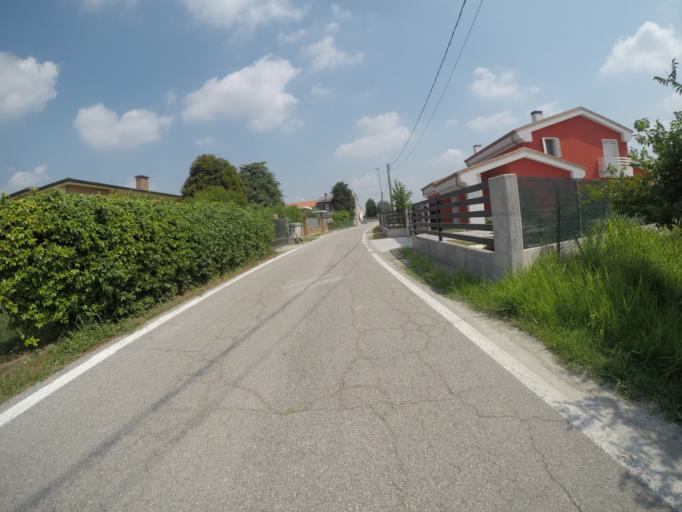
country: IT
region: Veneto
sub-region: Provincia di Rovigo
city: Villanova del Ghebbo Canton
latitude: 45.0585
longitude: 11.6372
